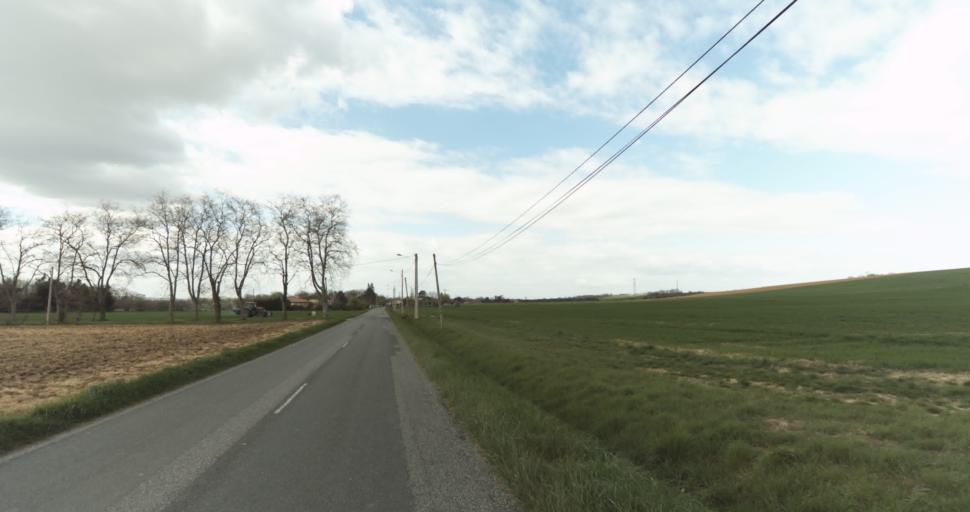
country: FR
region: Midi-Pyrenees
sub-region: Departement de la Haute-Garonne
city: Auterive
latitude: 43.3744
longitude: 1.4658
